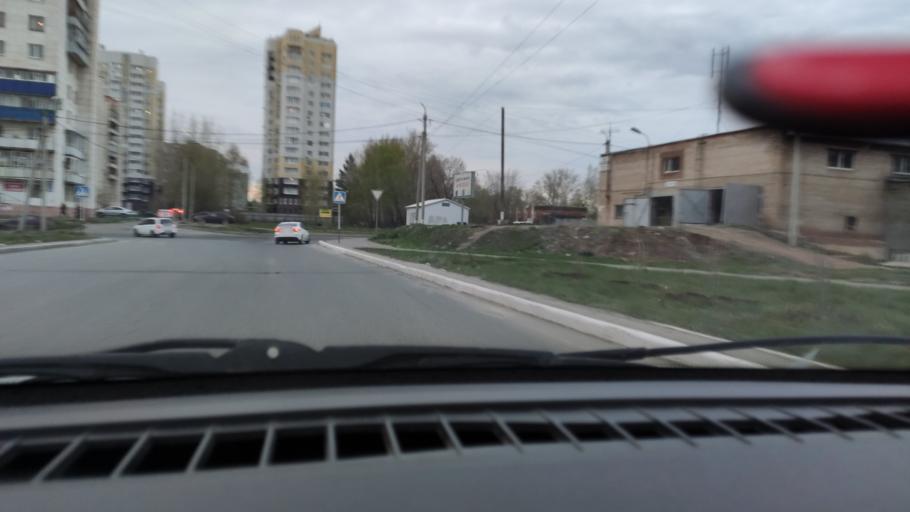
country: RU
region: Orenburg
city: Orenburg
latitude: 51.8141
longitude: 55.1474
